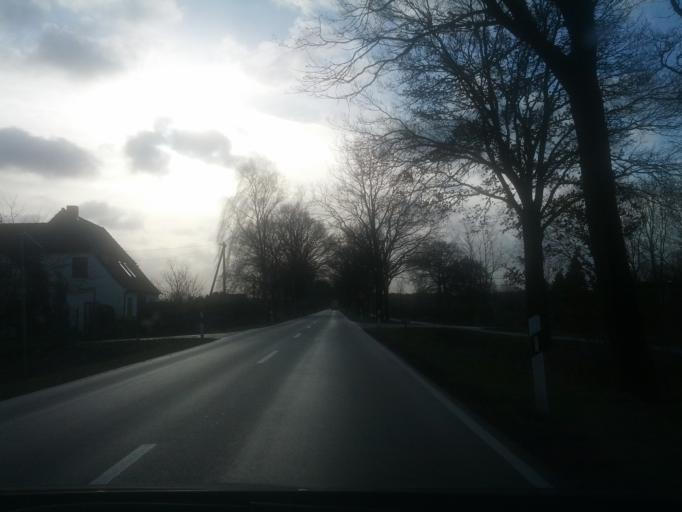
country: DE
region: Lower Saxony
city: Helvesiek
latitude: 53.2309
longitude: 9.4844
